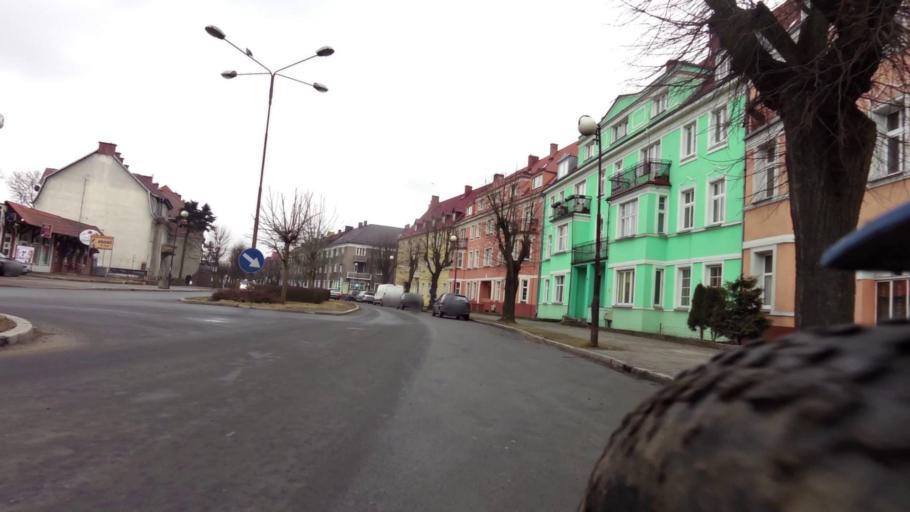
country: PL
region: West Pomeranian Voivodeship
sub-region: Powiat walecki
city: Walcz
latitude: 53.2746
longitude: 16.4821
